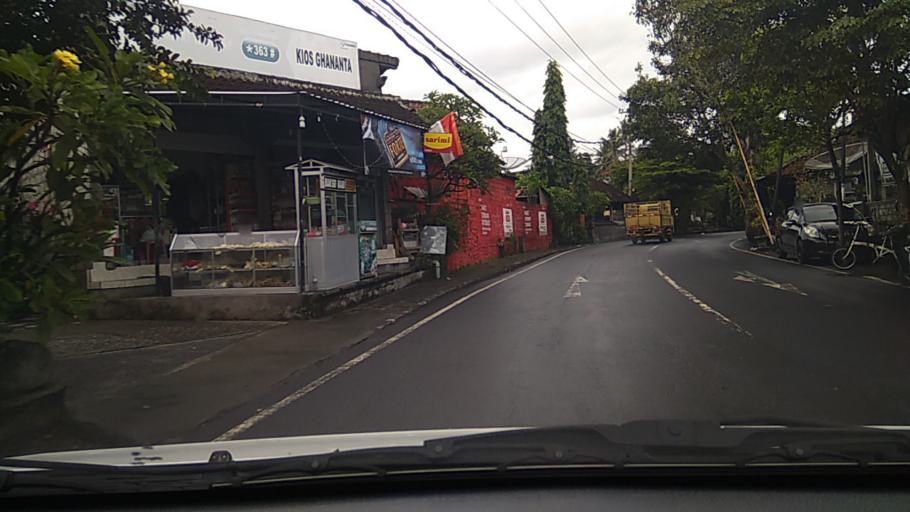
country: ID
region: Bali
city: Banjar Budakeling
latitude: -8.4353
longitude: 115.5896
